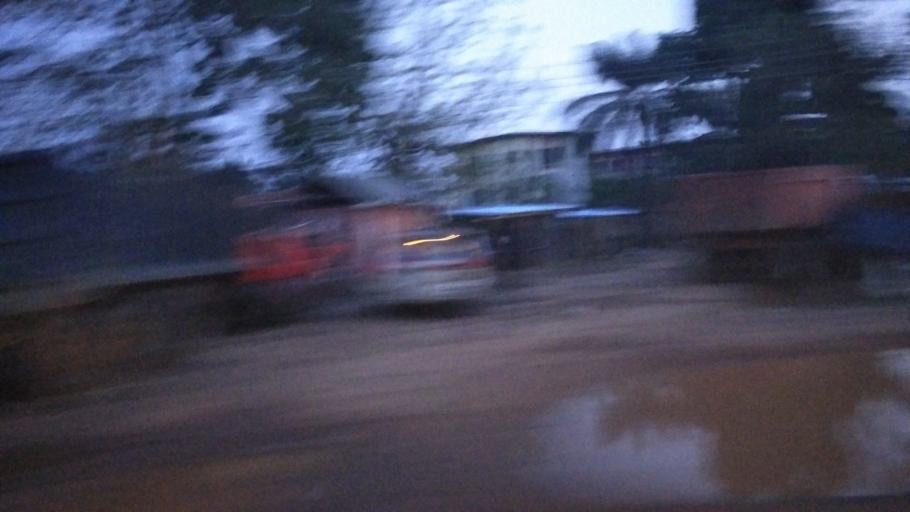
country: NG
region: Enugu
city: Enugu
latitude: 6.4661
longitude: 7.5953
